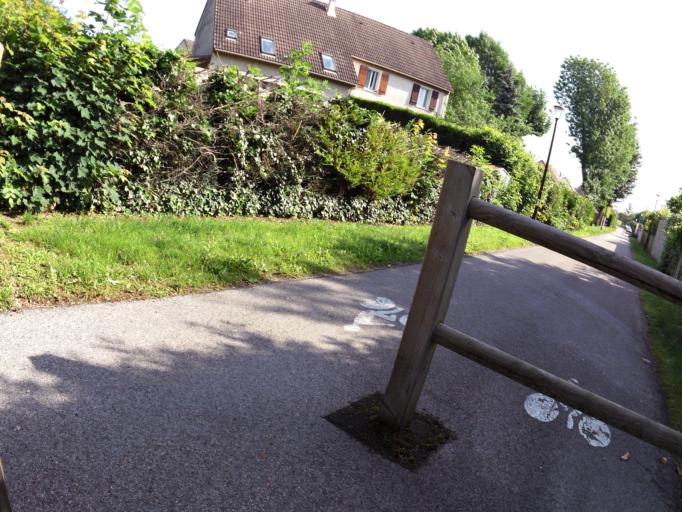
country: FR
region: Champagne-Ardenne
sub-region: Departement de l'Aube
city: Saint-Julien-les-Villas
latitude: 48.2748
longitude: 4.1005
